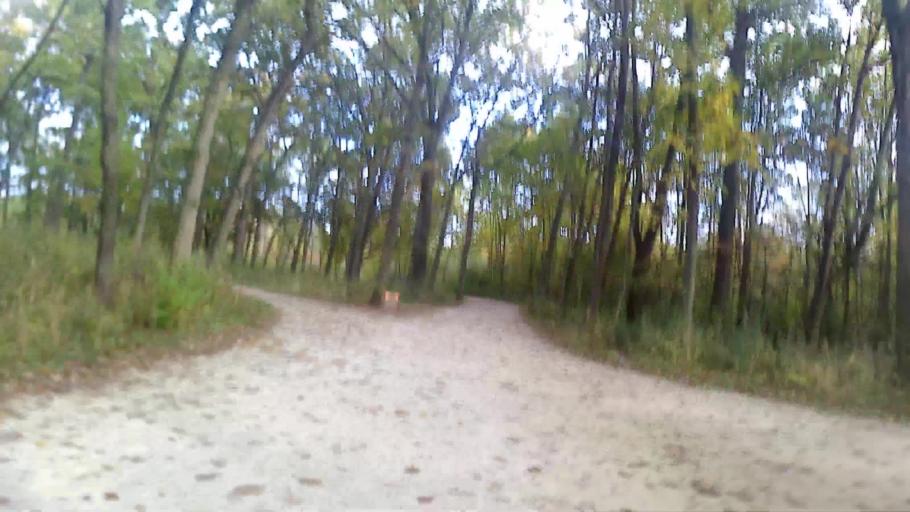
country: US
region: Illinois
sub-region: DuPage County
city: Warrenville
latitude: 41.8263
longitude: -88.1454
